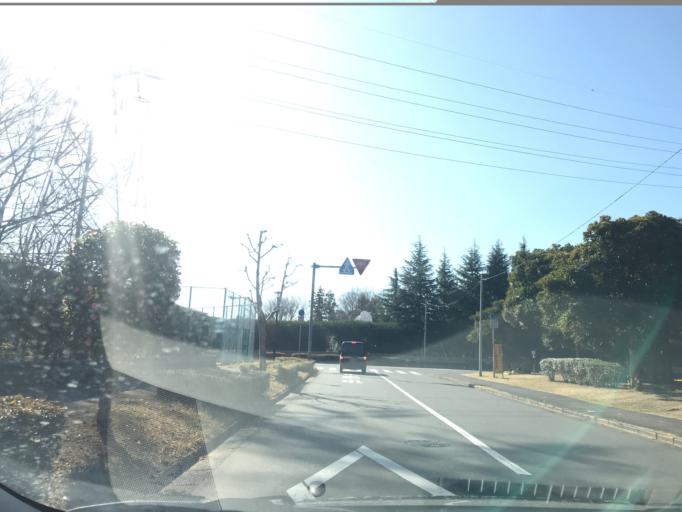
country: JP
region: Ibaraki
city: Tsukuba
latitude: 36.1264
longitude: 140.0893
